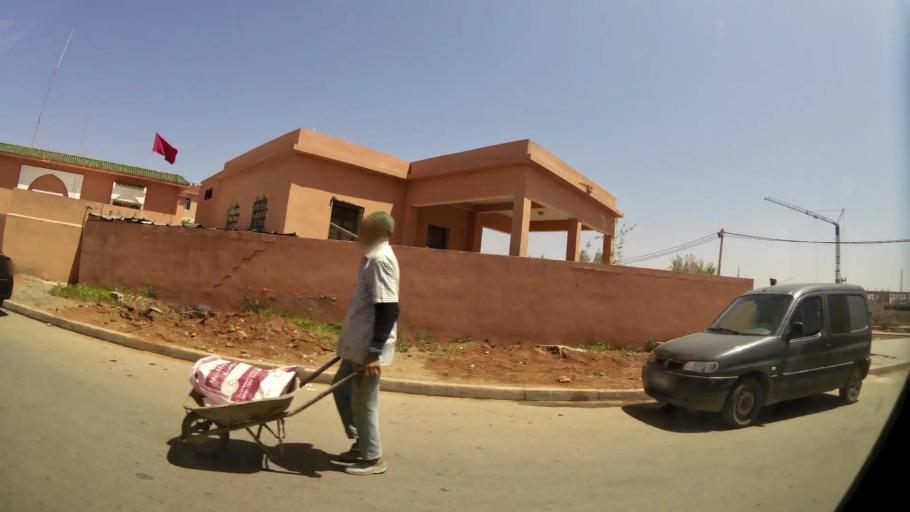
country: MA
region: Souss-Massa-Draa
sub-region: Inezgane-Ait Mellou
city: Inezgane
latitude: 30.3436
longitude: -9.4926
